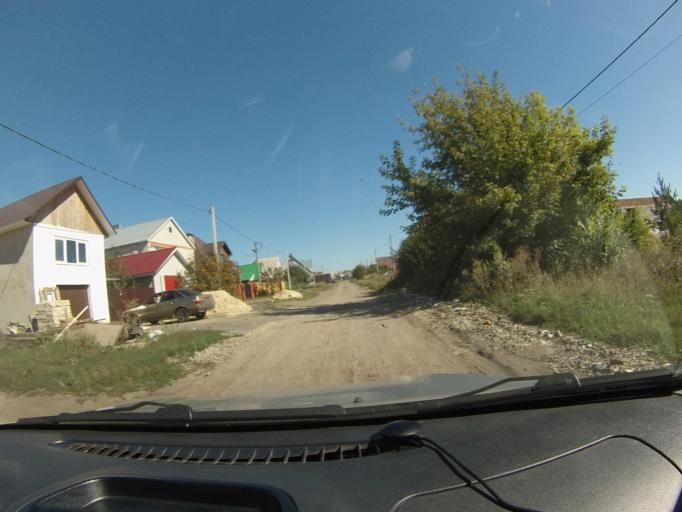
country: RU
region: Tambov
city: Komsomolets
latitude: 52.7609
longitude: 41.3647
